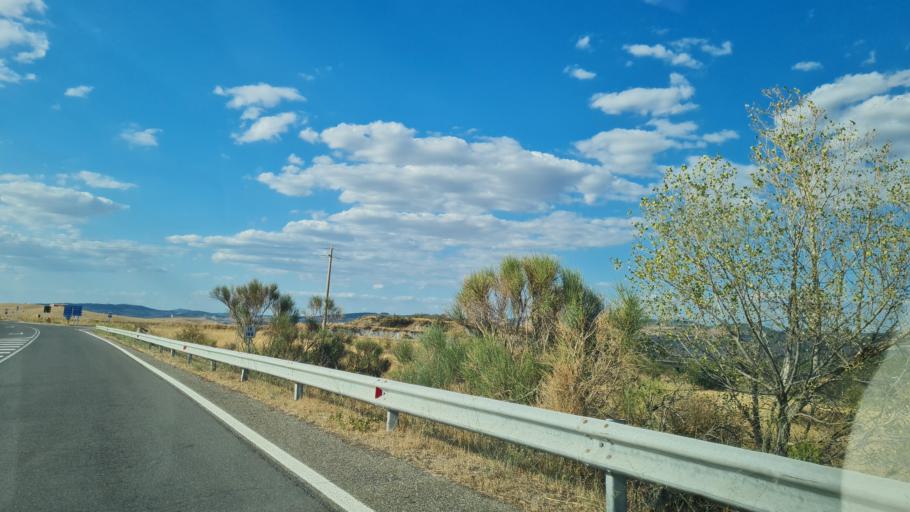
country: IT
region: Tuscany
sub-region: Provincia di Siena
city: Castiglione d'Orcia
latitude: 42.9788
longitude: 11.7064
